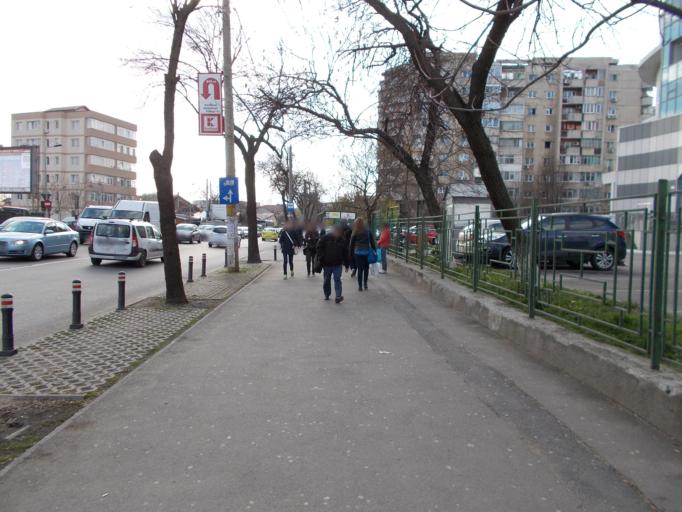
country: RO
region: Ilfov
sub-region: Comuna Popesti-Leordeni
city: Popesti-Leordeni
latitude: 44.3797
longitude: 26.1332
